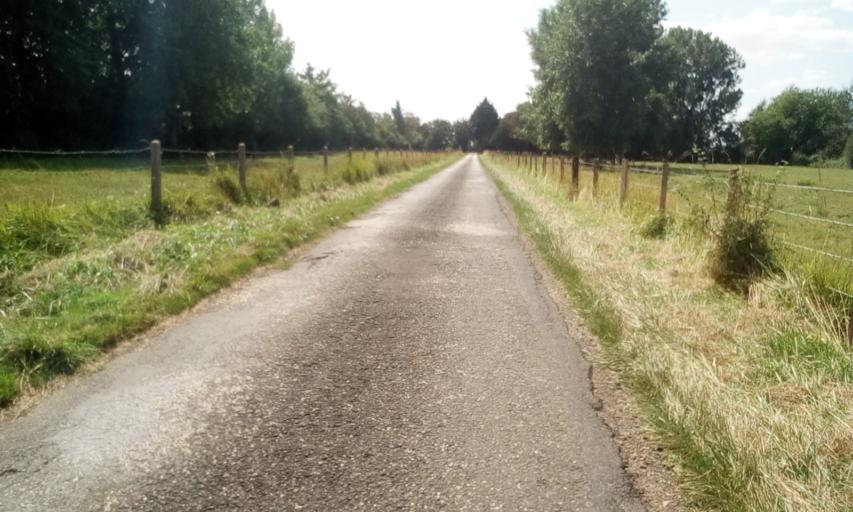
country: FR
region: Lower Normandy
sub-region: Departement du Calvados
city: Bellengreville
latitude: 49.1361
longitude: -0.2242
